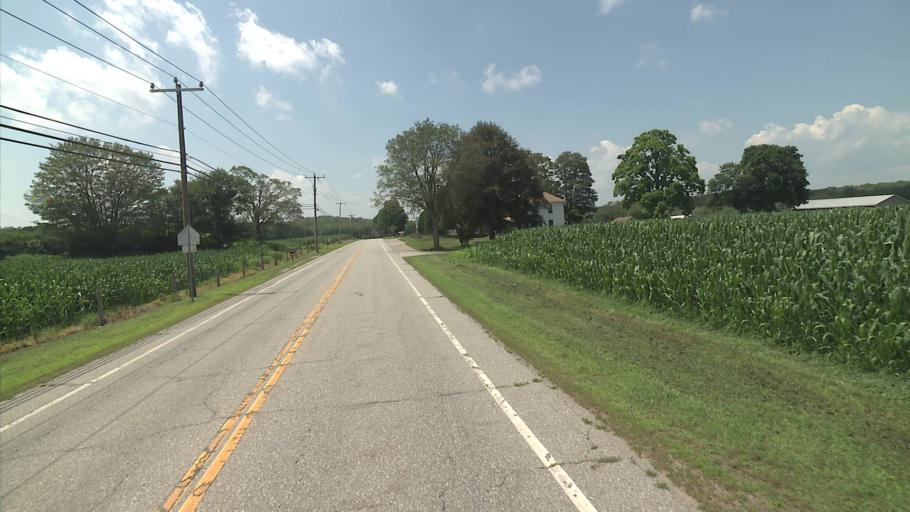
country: US
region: Connecticut
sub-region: New London County
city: Preston City
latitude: 41.5290
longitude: -71.9864
